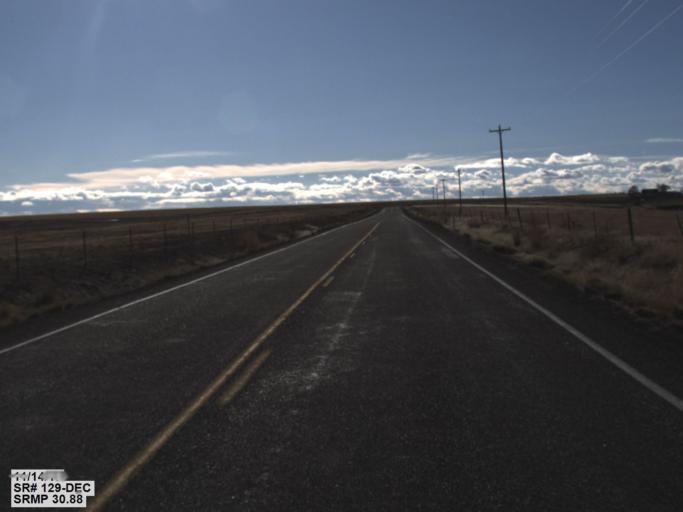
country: US
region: Washington
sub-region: Asotin County
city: Asotin
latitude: 46.3037
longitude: -117.0435
